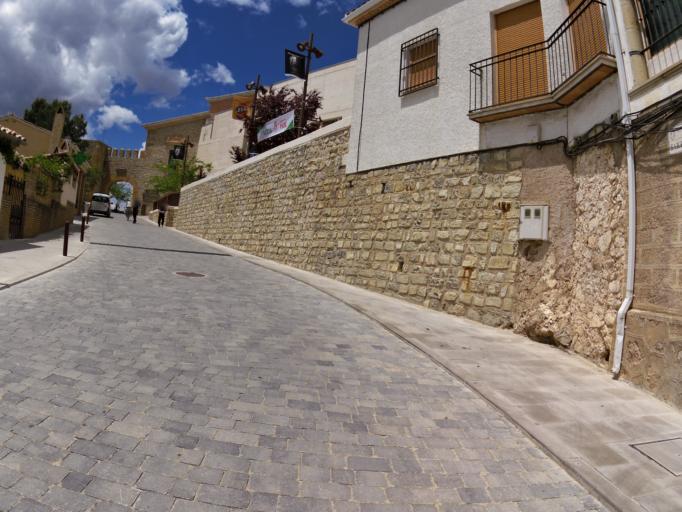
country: ES
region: Andalusia
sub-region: Provincia de Jaen
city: Segura de la Sierra
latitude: 38.2974
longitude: -2.6510
